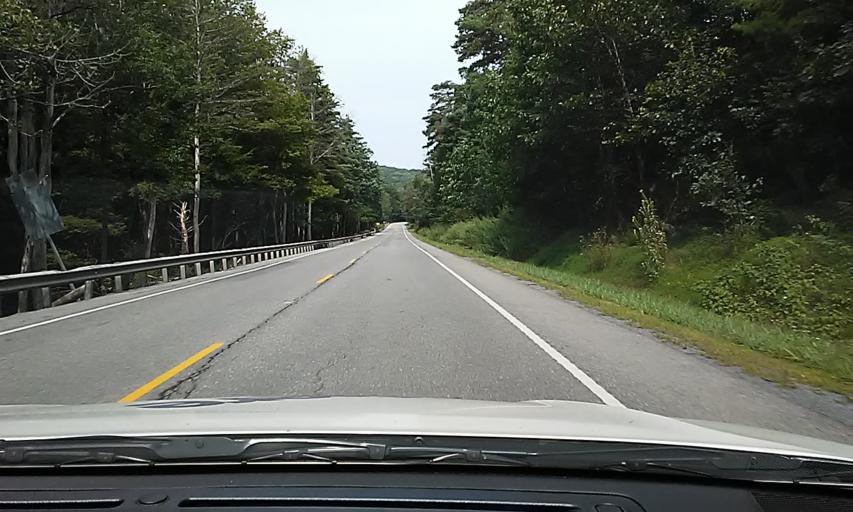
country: US
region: Pennsylvania
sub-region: Clearfield County
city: Treasure Lake
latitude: 41.2295
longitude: -78.6074
